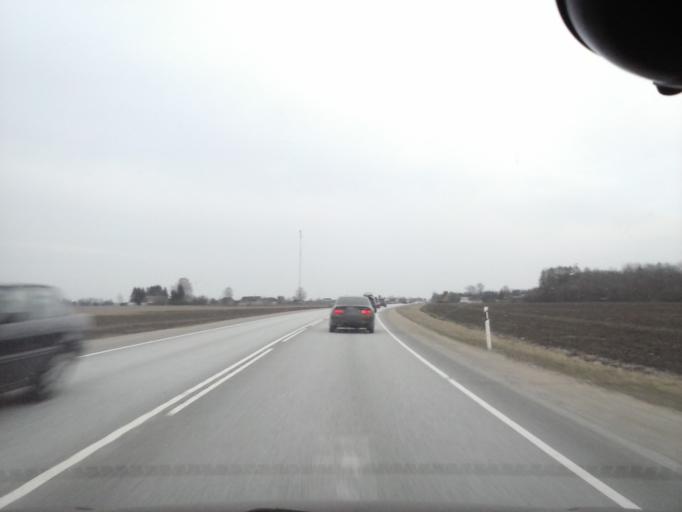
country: EE
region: Jogevamaa
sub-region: Poltsamaa linn
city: Poltsamaa
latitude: 58.6701
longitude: 25.9681
